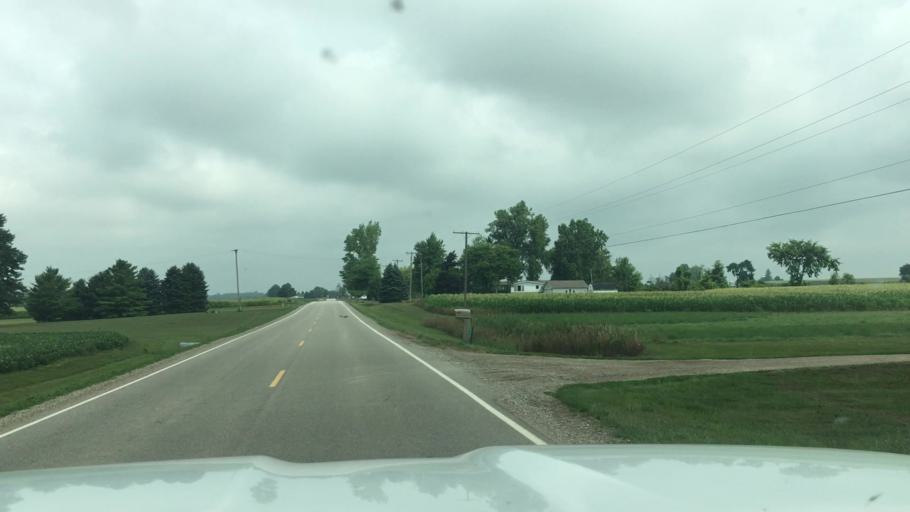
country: US
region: Michigan
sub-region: Sanilac County
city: Marlette
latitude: 43.3196
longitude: -82.9840
